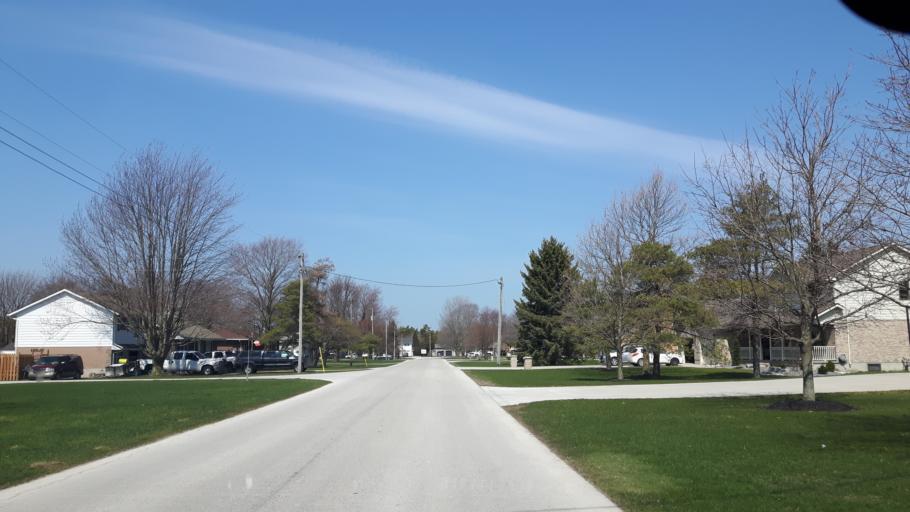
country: CA
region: Ontario
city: Goderich
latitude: 43.7250
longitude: -81.6843
